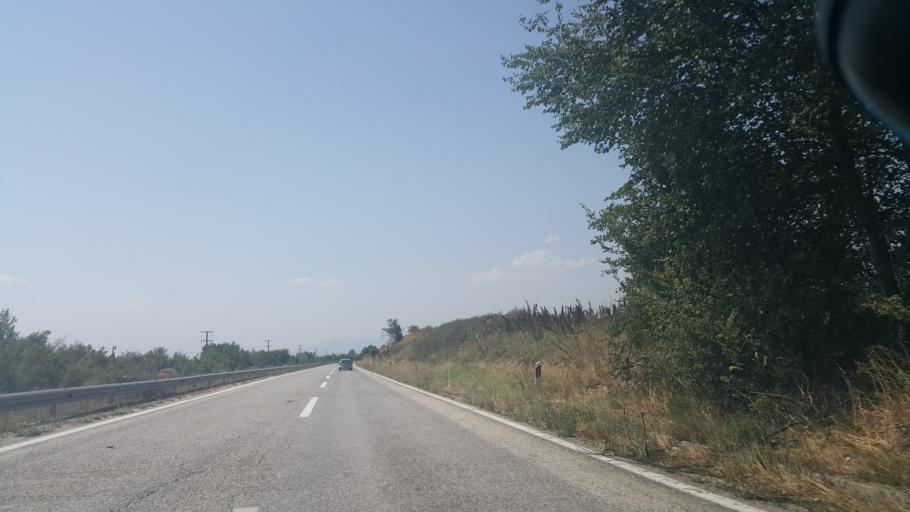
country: MK
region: Petrovec
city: Petrovec
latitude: 41.9092
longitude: 21.6489
